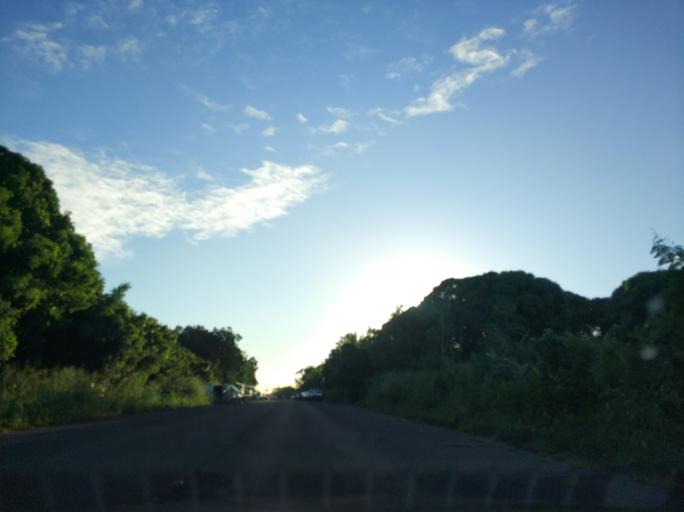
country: US
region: Hawaii
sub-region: Hawaii County
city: Leilani Estates
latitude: 19.3579
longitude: -154.9836
